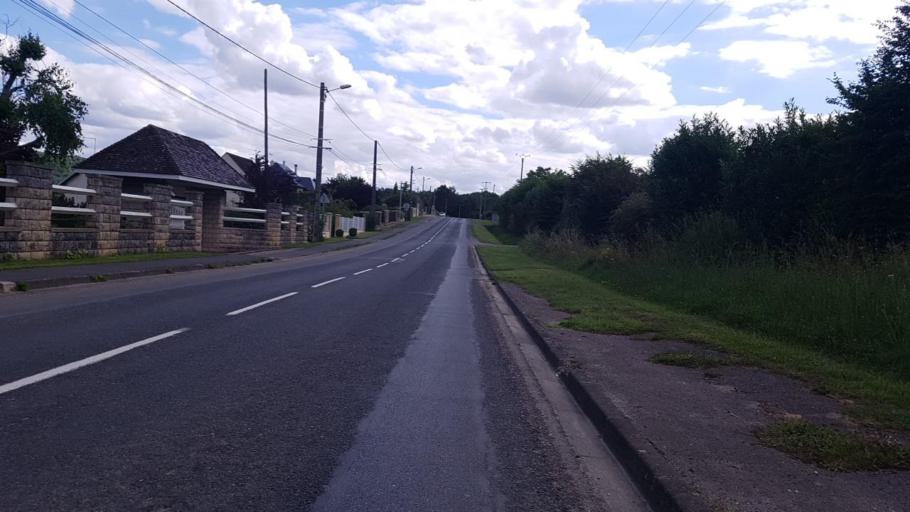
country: FR
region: Picardie
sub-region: Departement de l'Aisne
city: Crezancy
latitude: 49.0821
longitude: 3.5280
